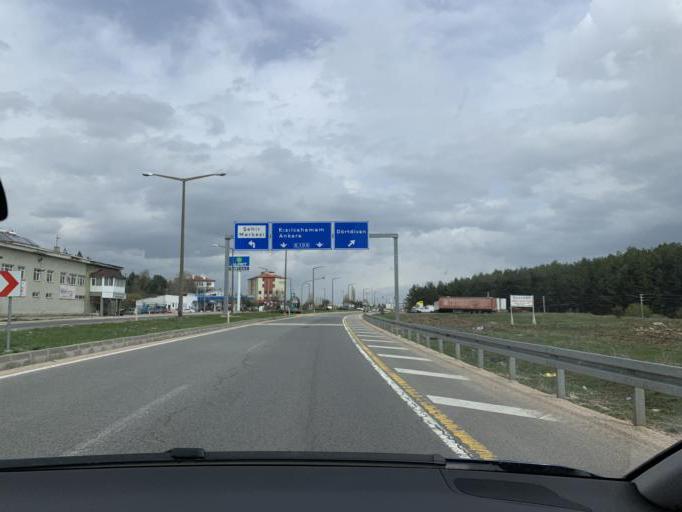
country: TR
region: Bolu
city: Gerede
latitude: 40.7995
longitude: 32.1816
